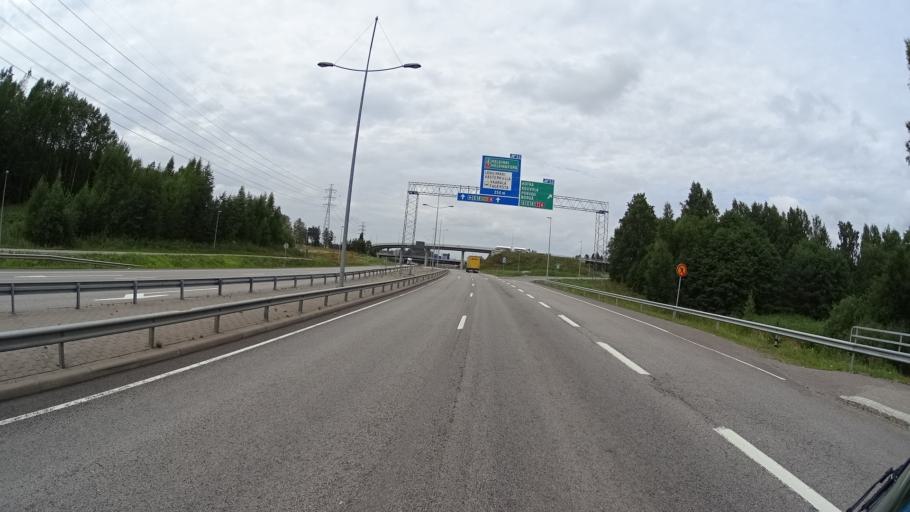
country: FI
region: Uusimaa
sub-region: Helsinki
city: Vantaa
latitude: 60.2550
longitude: 25.1299
